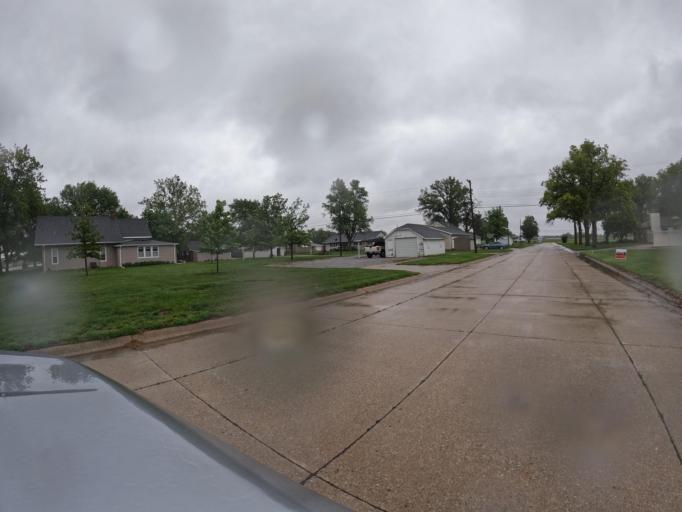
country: US
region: Nebraska
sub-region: Saline County
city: Wilber
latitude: 40.3944
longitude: -96.9239
